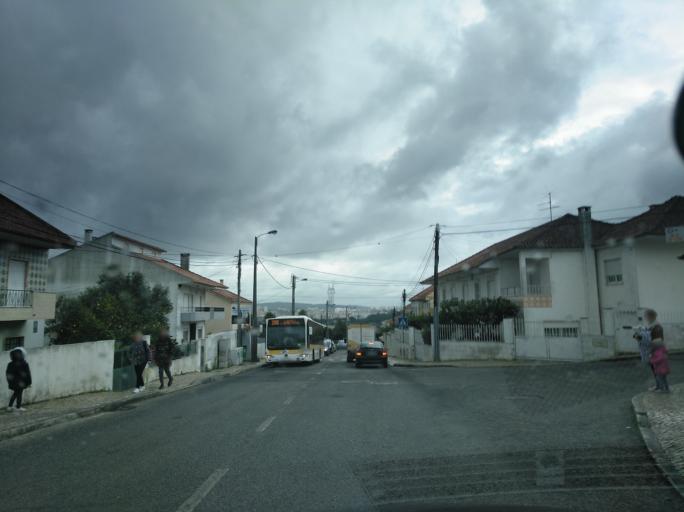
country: PT
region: Lisbon
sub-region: Odivelas
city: Famoes
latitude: 38.7884
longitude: -9.2094
